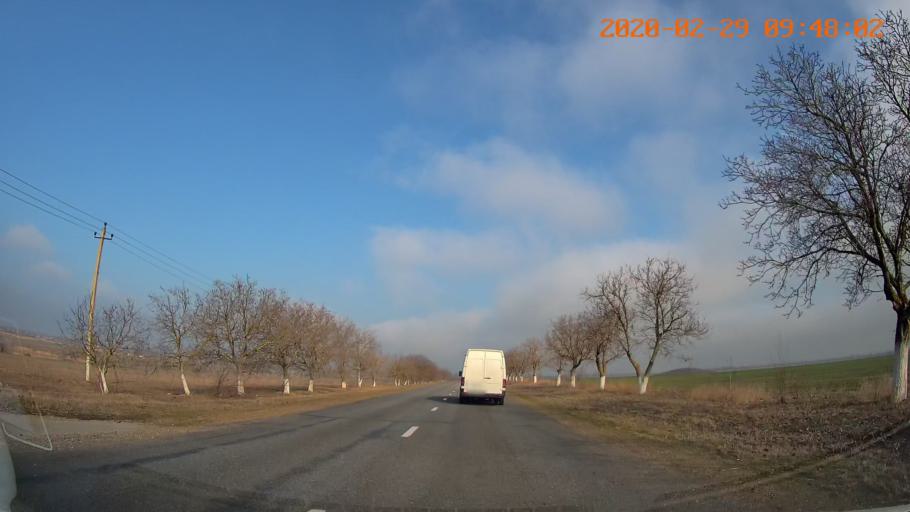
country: MD
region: Telenesti
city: Crasnoe
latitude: 46.6830
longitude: 29.7870
